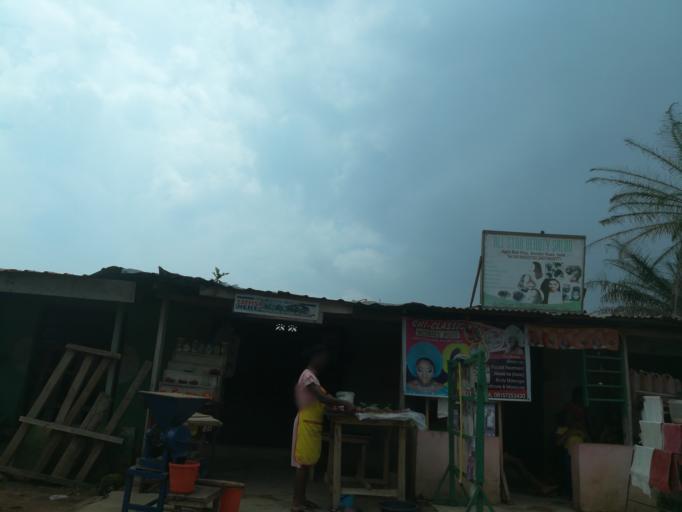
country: NG
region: Lagos
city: Ikorodu
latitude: 6.5708
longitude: 3.5919
